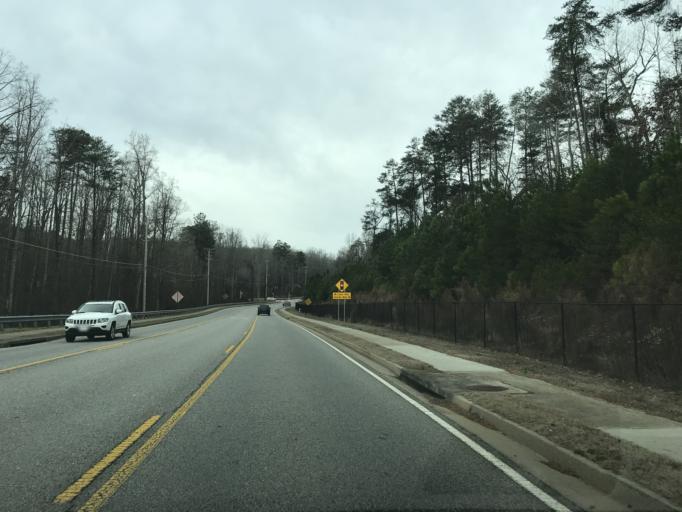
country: US
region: Georgia
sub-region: Forsyth County
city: Cumming
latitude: 34.2235
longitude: -84.1169
